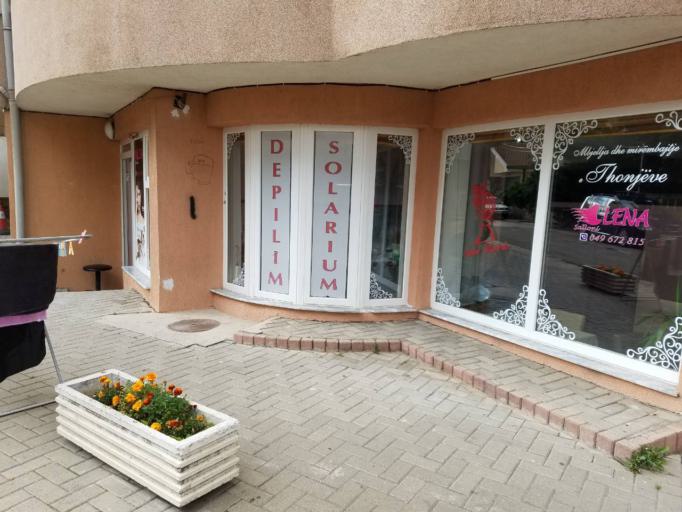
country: XK
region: Pristina
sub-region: Komuna e Prishtines
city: Pristina
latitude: 42.6537
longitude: 21.1711
